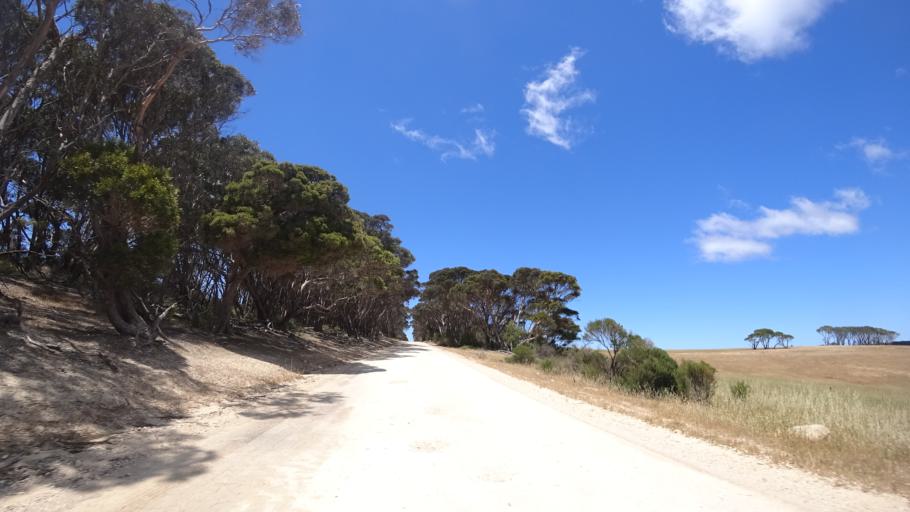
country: AU
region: South Australia
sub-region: Yankalilla
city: Normanville
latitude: -35.8187
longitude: 138.0772
